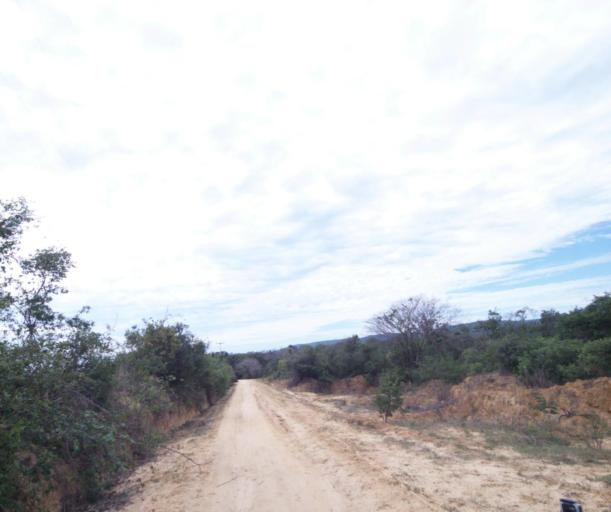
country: BR
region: Bahia
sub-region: Carinhanha
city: Carinhanha
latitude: -14.2535
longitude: -44.3644
